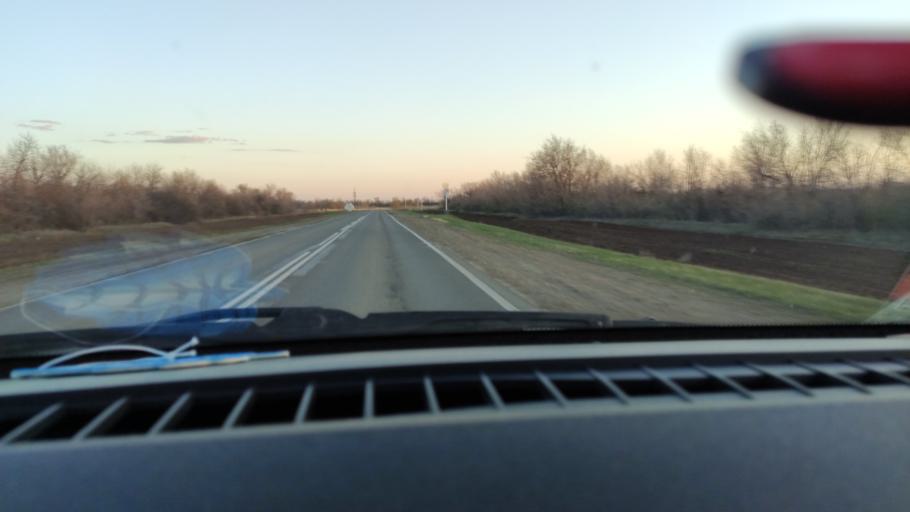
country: RU
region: Saratov
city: Privolzhskiy
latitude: 51.3329
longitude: 46.0370
